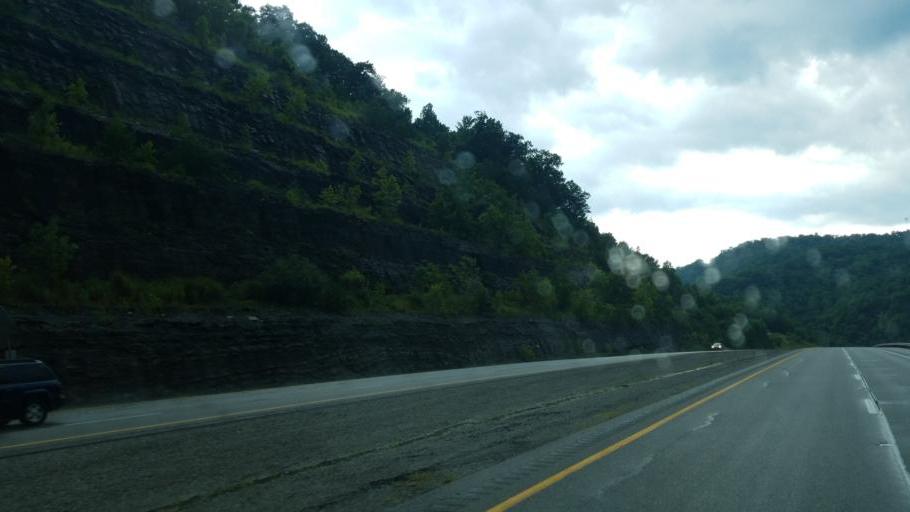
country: US
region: Kentucky
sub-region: Pike County
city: Pikeville
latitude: 37.5142
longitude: -82.4659
